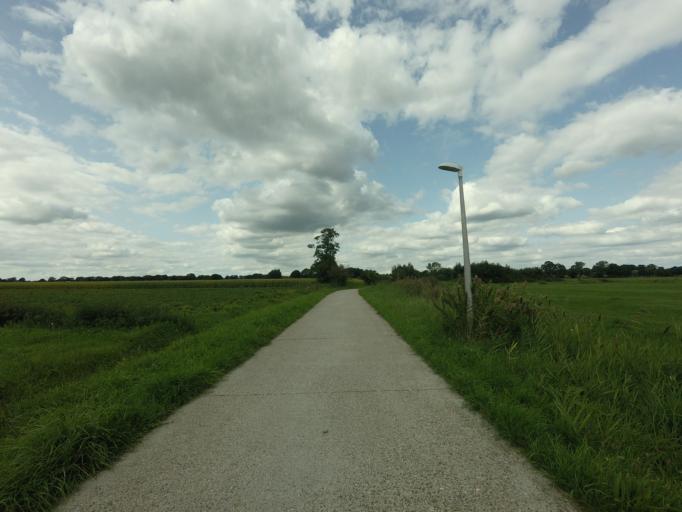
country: NL
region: Drenthe
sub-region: Gemeente De Wolden
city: Ruinen
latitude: 52.7541
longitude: 6.3626
